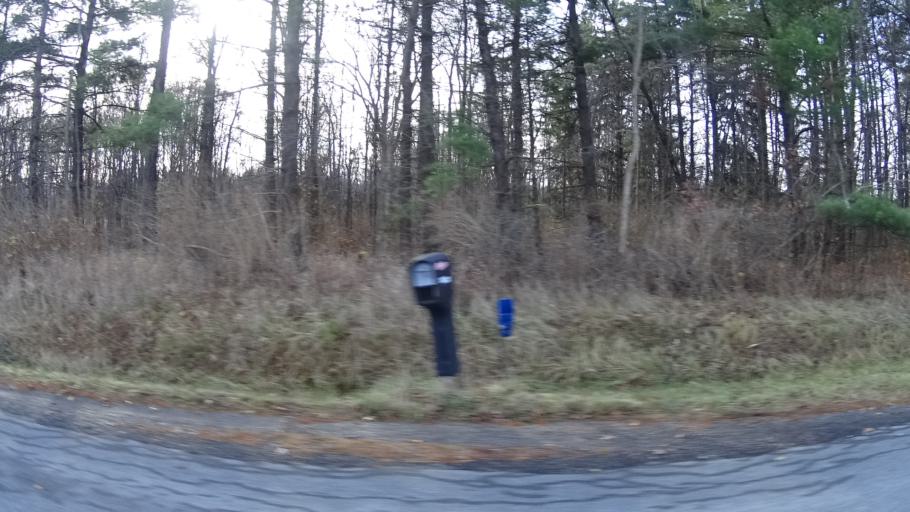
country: US
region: Ohio
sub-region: Lorain County
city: Grafton
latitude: 41.2076
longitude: -82.0283
